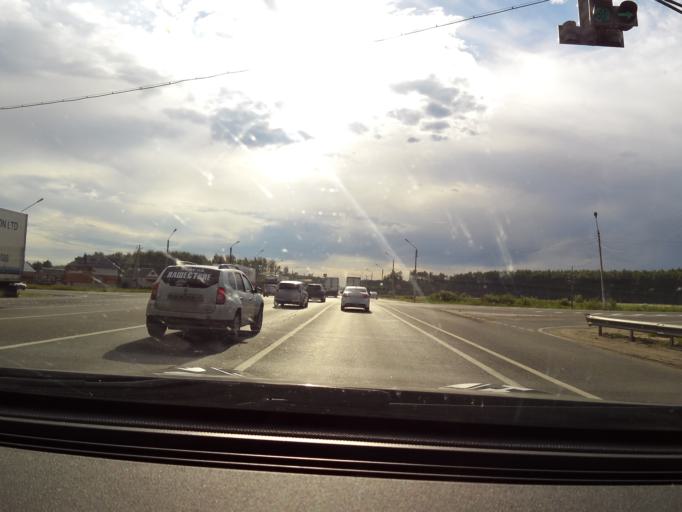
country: RU
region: Vladimir
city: Novovyazniki
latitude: 56.2194
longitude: 42.1850
